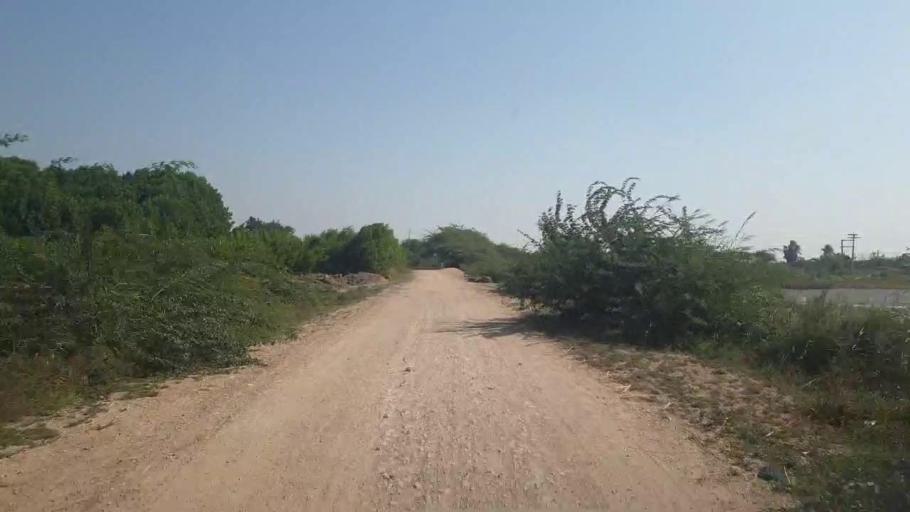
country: PK
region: Sindh
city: Badin
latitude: 24.6804
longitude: 68.8664
